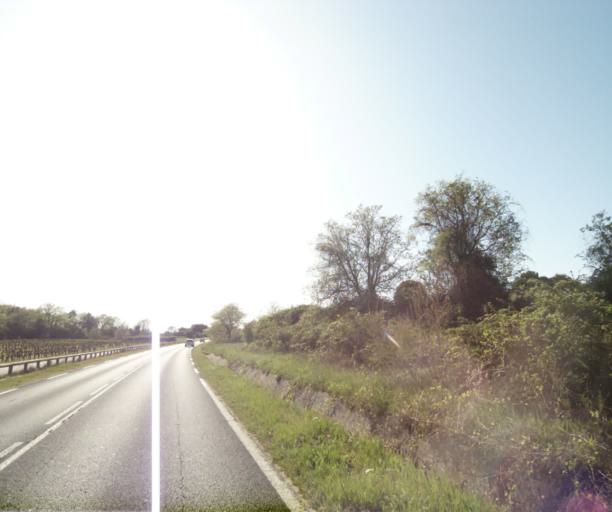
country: FR
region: Languedoc-Roussillon
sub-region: Departement de l'Herault
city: Juvignac
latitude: 43.6087
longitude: 3.7956
